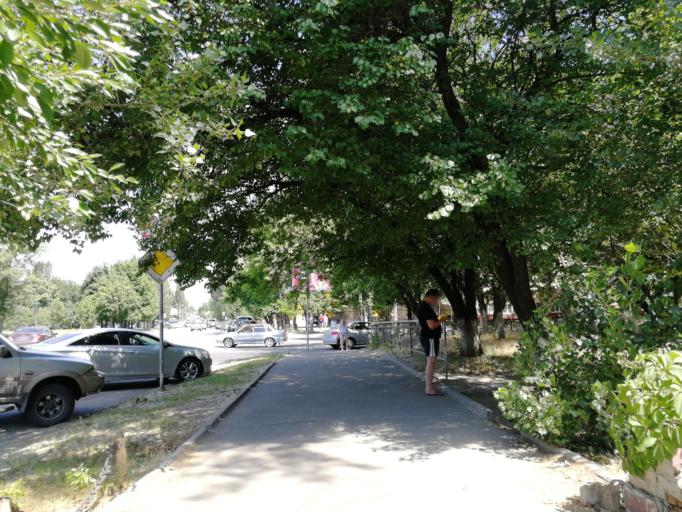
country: RU
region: Rostov
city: Rostov-na-Donu
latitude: 47.2141
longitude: 39.6350
